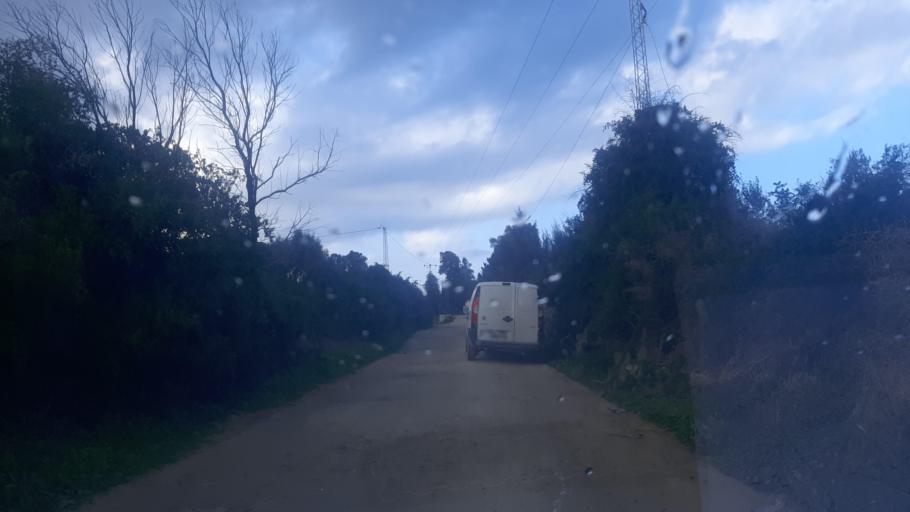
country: TN
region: Nabul
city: Manzil Bu Zalafah
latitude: 36.7394
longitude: 10.5303
